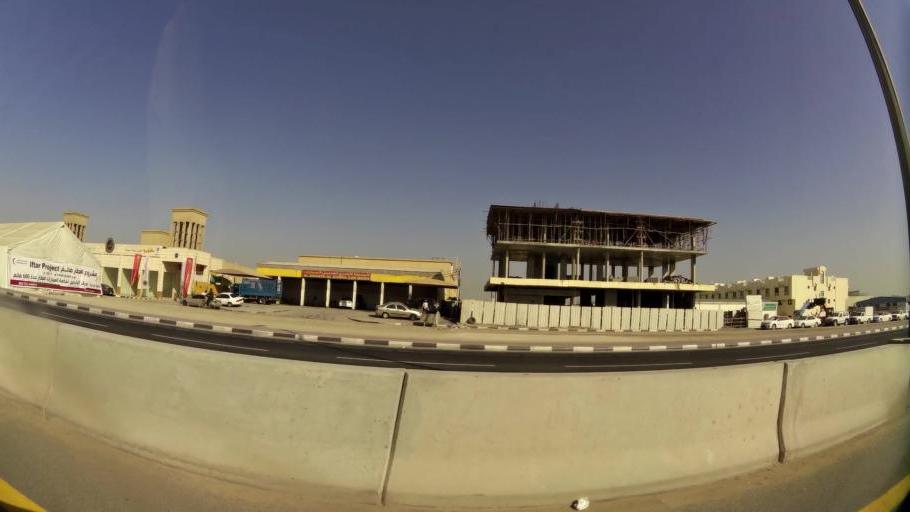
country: AE
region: Ash Shariqah
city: Sharjah
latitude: 25.3233
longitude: 55.4166
